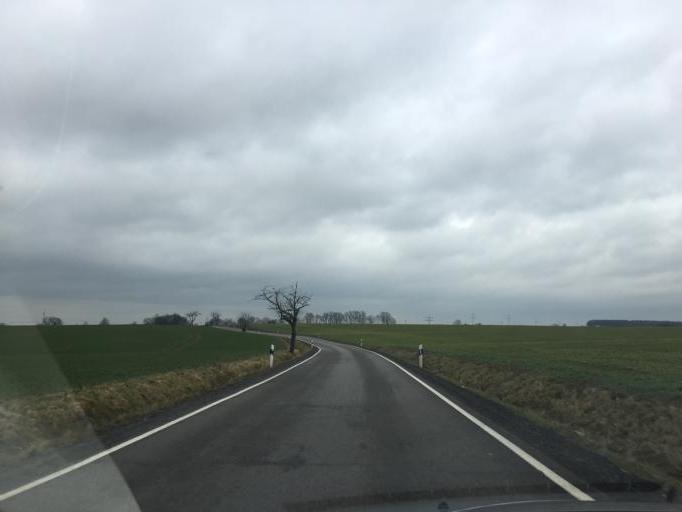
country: DE
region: Saxony
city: Pfaffroda
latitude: 50.8666
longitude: 12.5381
